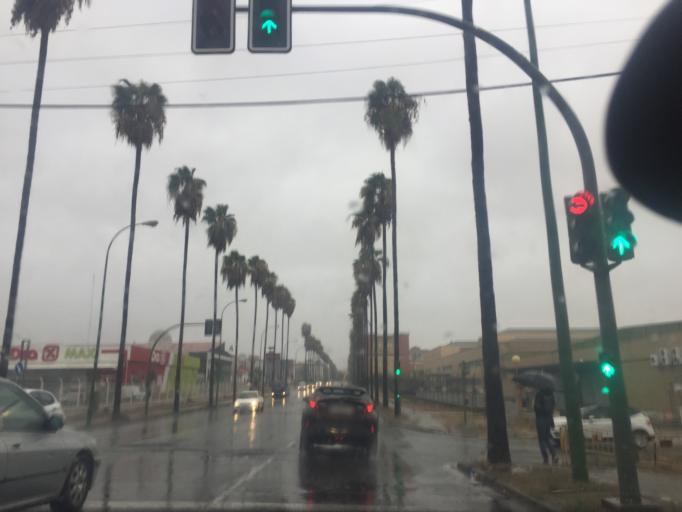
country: ES
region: Andalusia
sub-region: Provincia de Sevilla
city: Sevilla
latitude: 37.3641
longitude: -5.9566
